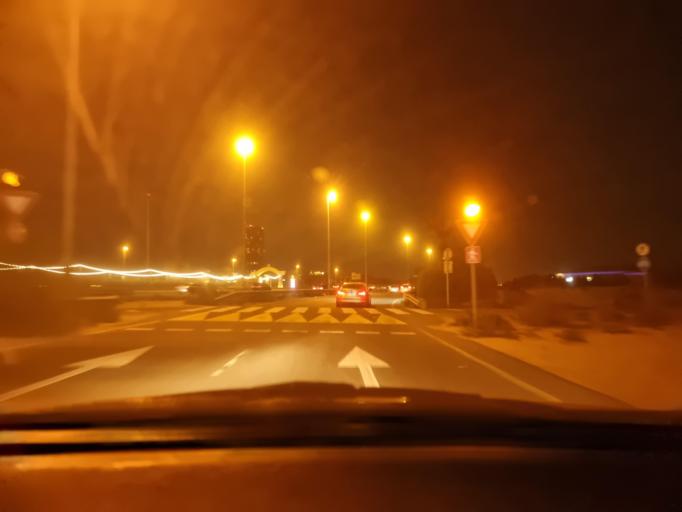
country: AE
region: Dubai
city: Dubai
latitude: 25.0769
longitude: 55.3086
